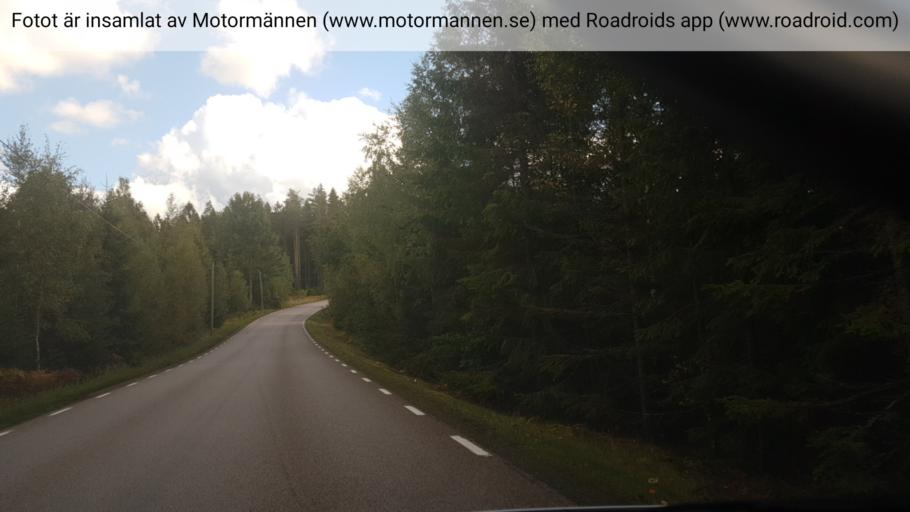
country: SE
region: Vaestra Goetaland
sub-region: Skovde Kommun
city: Stopen
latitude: 58.5394
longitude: 13.7062
